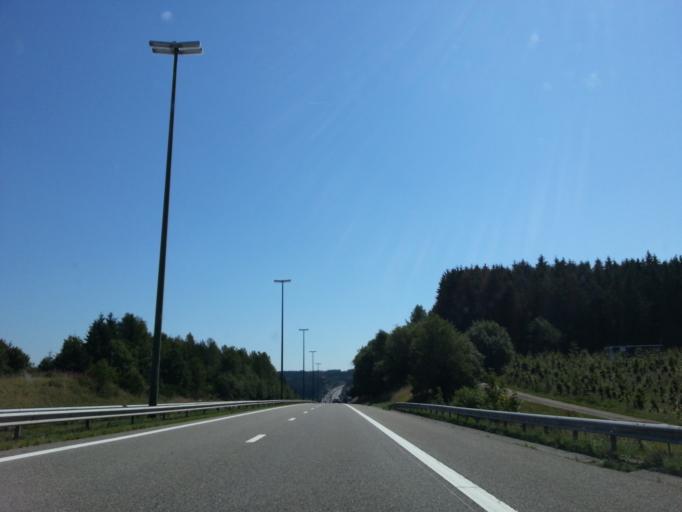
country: BE
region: Wallonia
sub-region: Province de Liege
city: Saint-Vith
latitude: 50.2619
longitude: 6.1363
